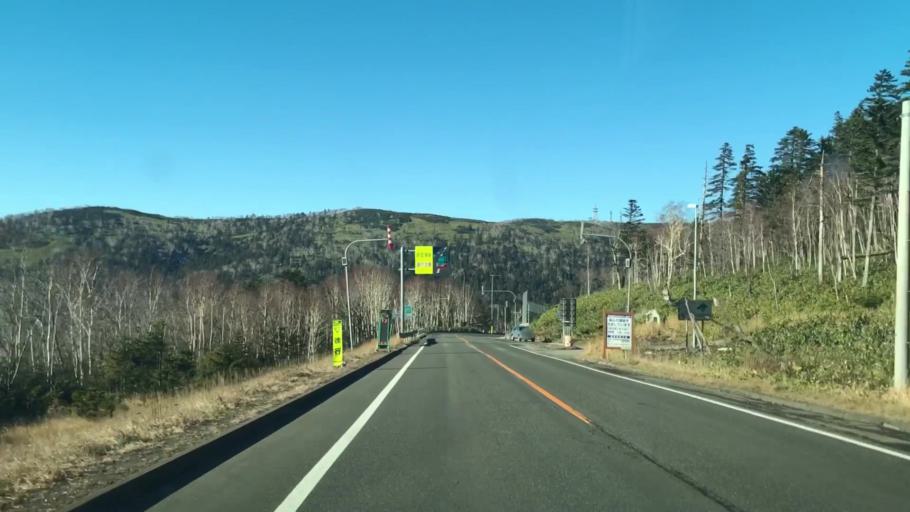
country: JP
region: Hokkaido
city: Otofuke
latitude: 42.9760
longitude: 142.7467
